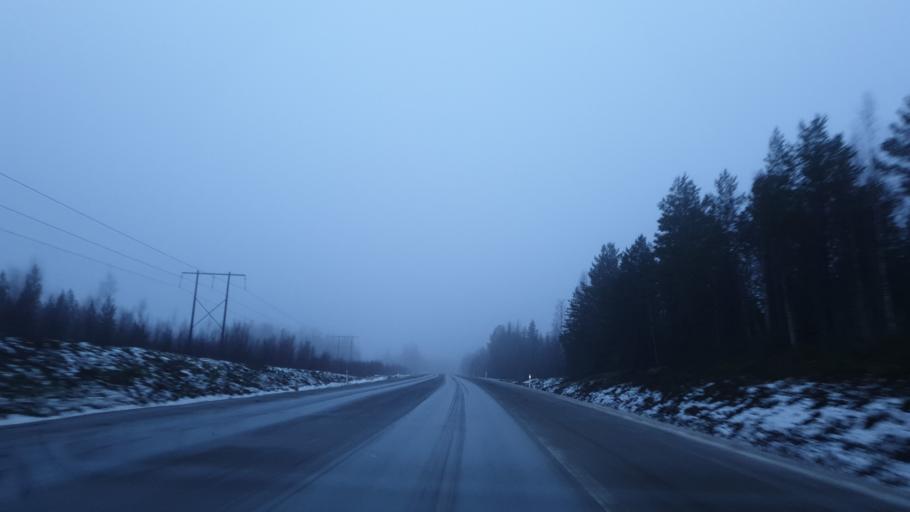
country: SE
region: Vaesterbotten
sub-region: Umea Kommun
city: Holmsund
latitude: 63.7507
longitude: 20.3707
